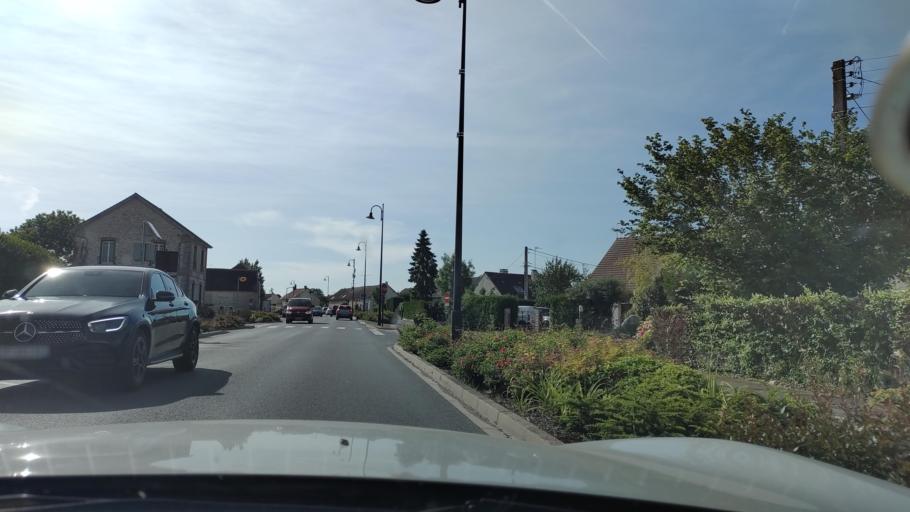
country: FR
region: Ile-de-France
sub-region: Departement de Seine-et-Marne
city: Sourdun
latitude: 48.5373
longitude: 3.3535
